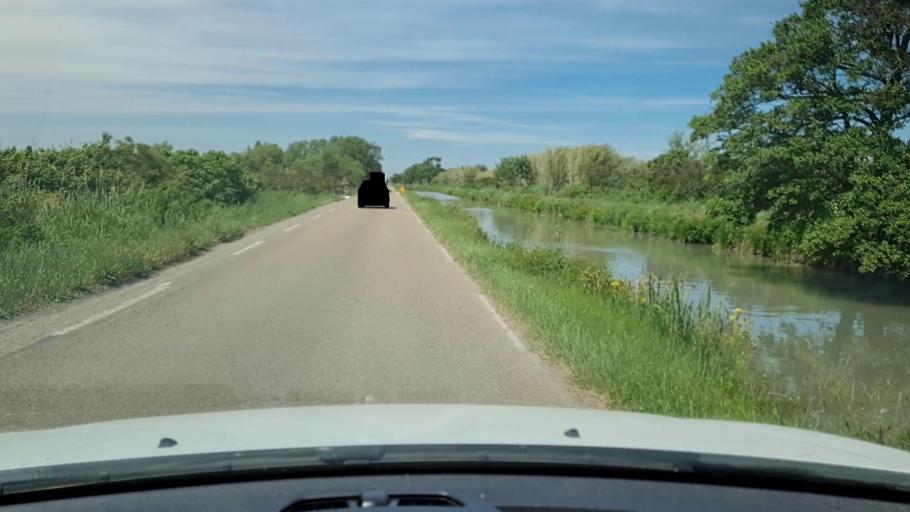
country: FR
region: Languedoc-Roussillon
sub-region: Departement du Gard
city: Saint-Gilles
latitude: 43.5847
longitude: 4.3470
